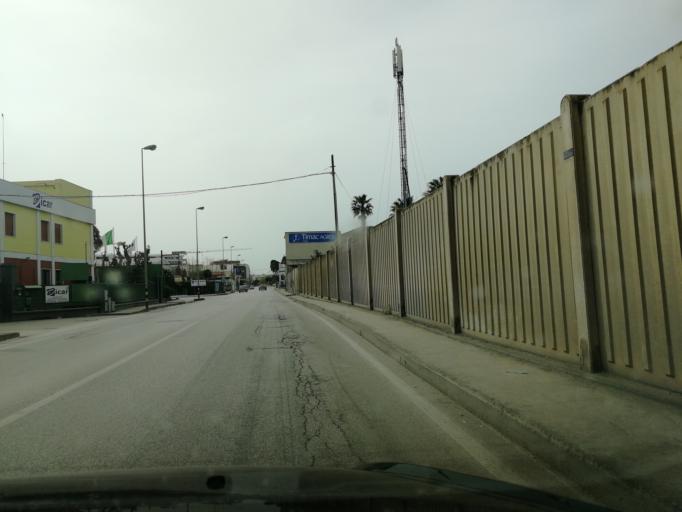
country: IT
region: Apulia
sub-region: Provincia di Barletta - Andria - Trani
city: Barletta
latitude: 41.3168
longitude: 16.2965
